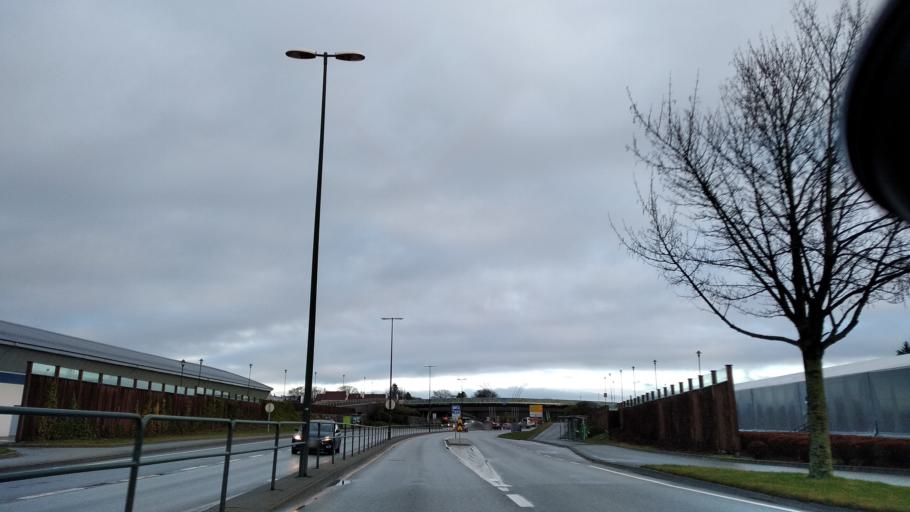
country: NO
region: Rogaland
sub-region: Stavanger
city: Stavanger
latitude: 58.9555
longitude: 5.6972
